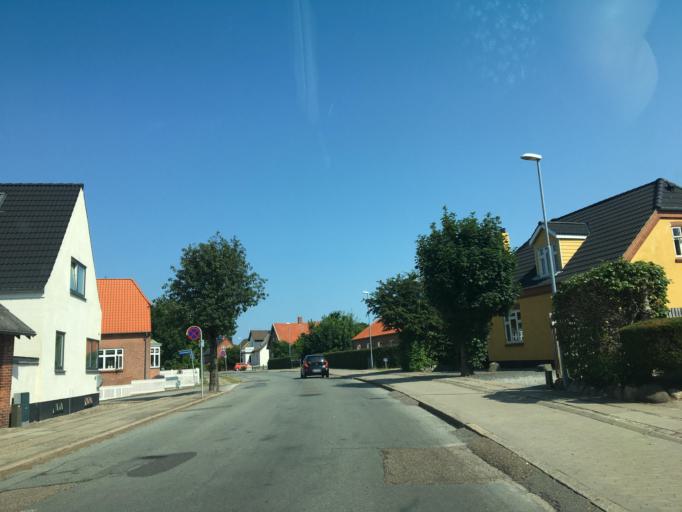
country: DK
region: North Denmark
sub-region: Thisted Kommune
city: Thisted
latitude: 56.9607
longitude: 8.6906
